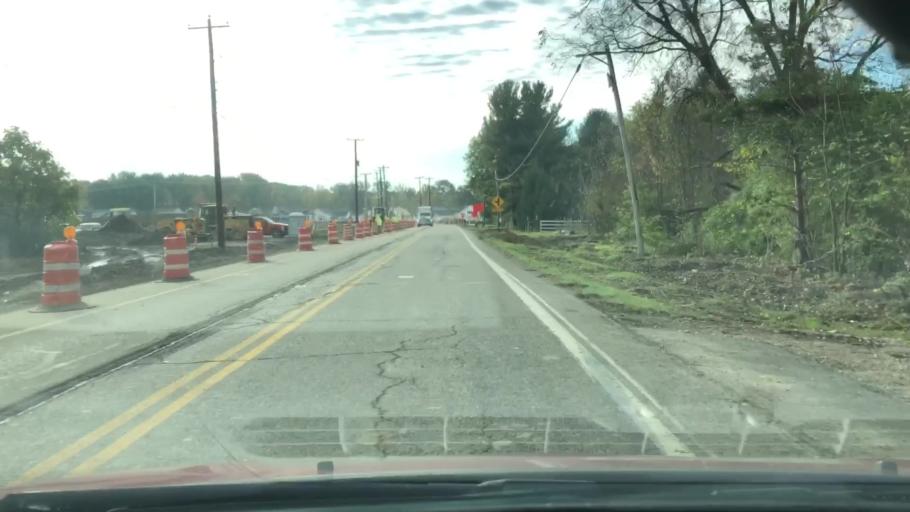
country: US
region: Ohio
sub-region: Franklin County
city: Huber Ridge
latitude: 40.0948
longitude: -82.8669
